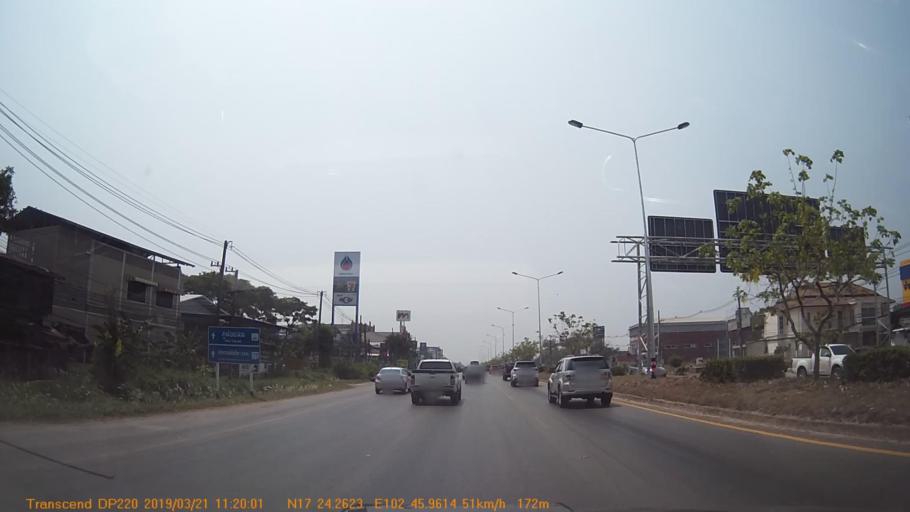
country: TH
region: Changwat Udon Thani
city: Udon Thani
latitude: 17.4043
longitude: 102.7660
